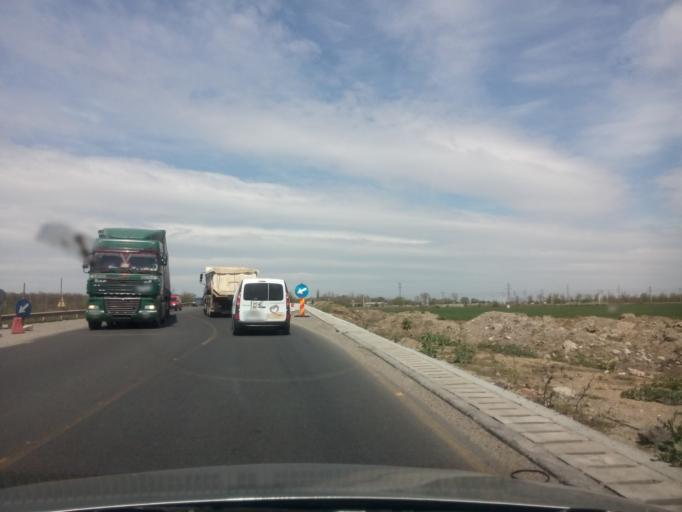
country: RO
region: Ilfov
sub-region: Comuna Pantelimon
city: Pantelimon
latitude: 44.4702
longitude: 26.2320
